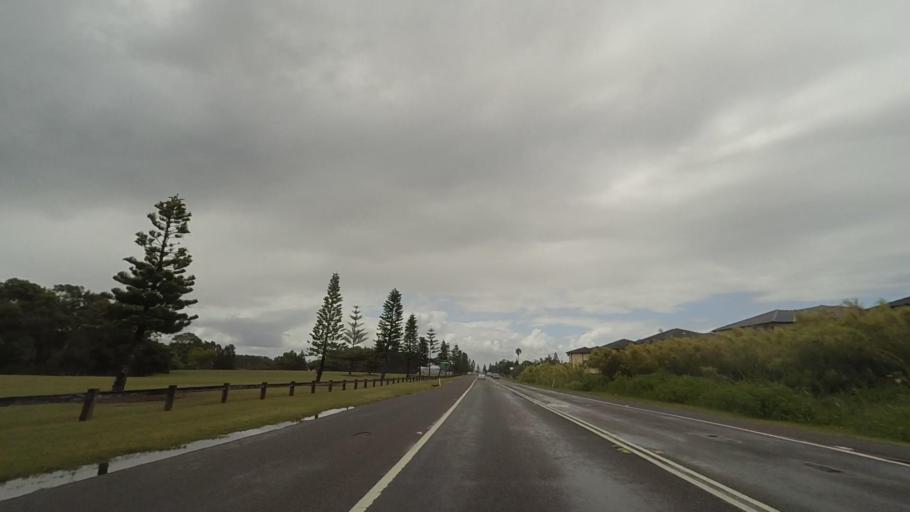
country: AU
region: New South Wales
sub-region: Wyong Shire
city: The Entrance
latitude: -33.3329
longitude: 151.5035
